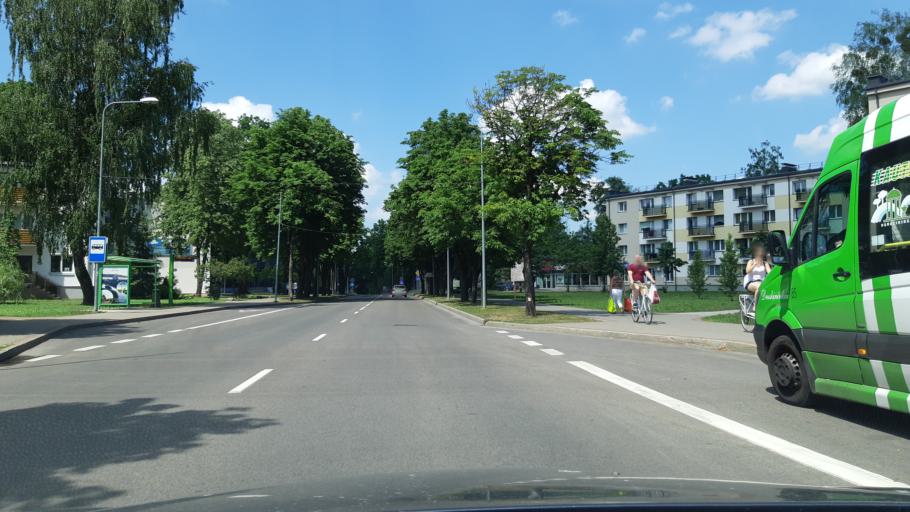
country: LT
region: Alytaus apskritis
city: Druskininkai
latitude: 54.0139
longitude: 23.9837
